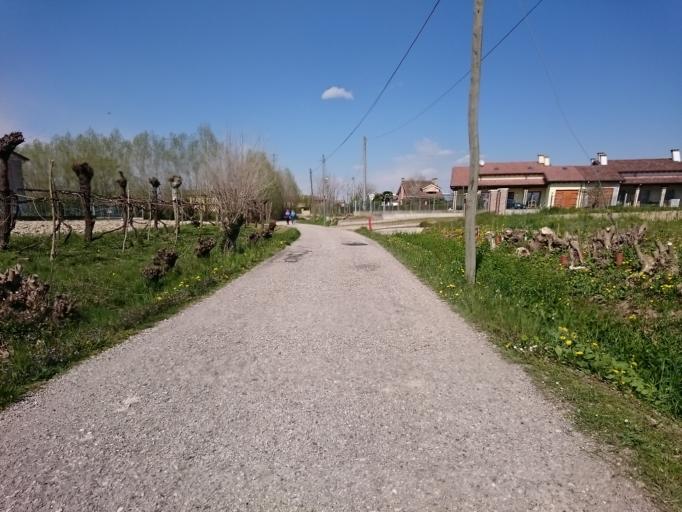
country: IT
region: Veneto
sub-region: Provincia di Padova
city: Polverara
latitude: 45.3103
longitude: 11.9714
